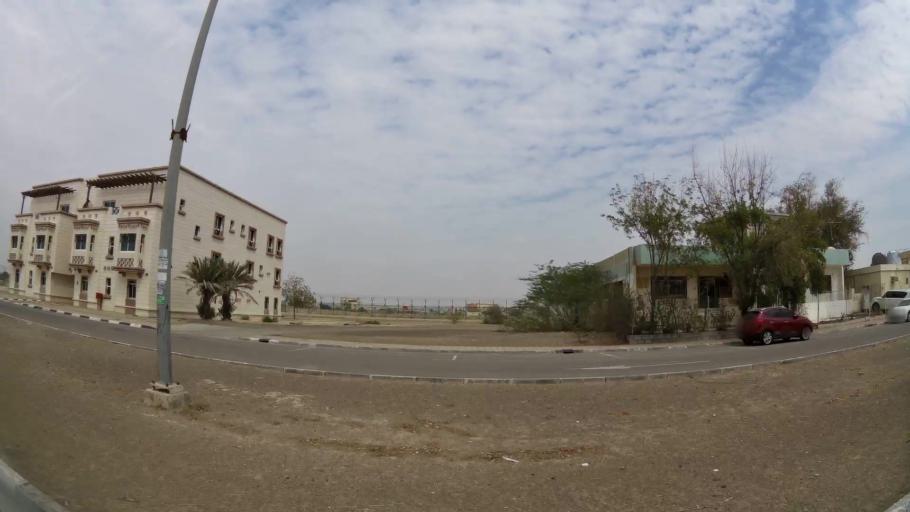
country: OM
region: Al Buraimi
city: Al Buraymi
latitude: 24.2250
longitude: 55.7898
